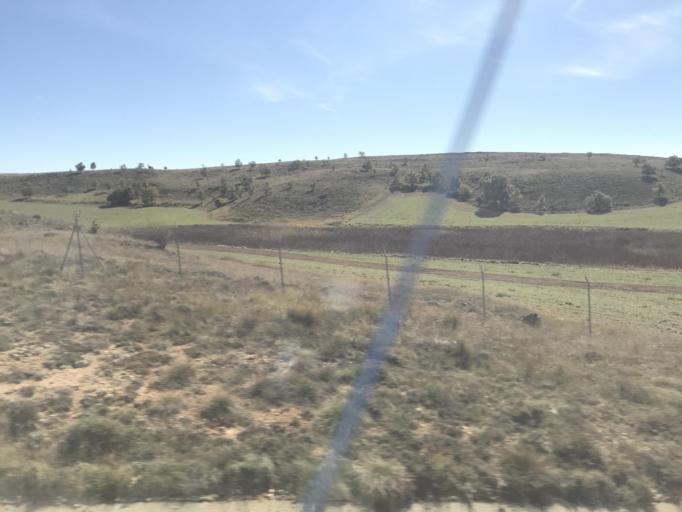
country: ES
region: Castille-La Mancha
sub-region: Provincia de Guadalajara
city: Anguita
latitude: 41.0960
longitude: -2.3890
